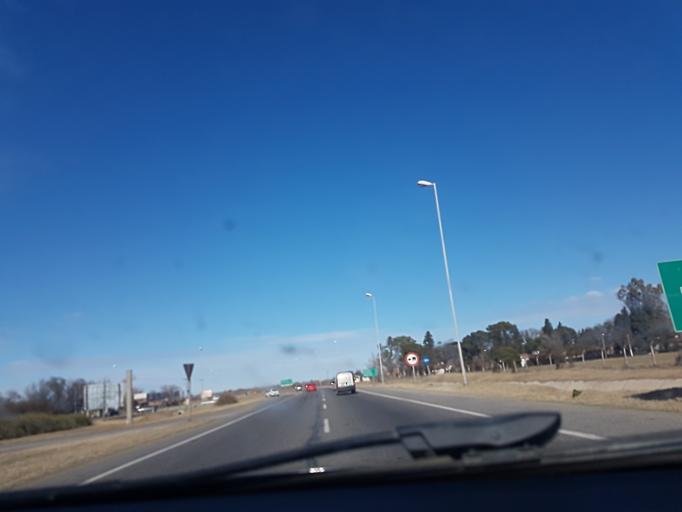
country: AR
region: Cordoba
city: La Calera
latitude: -31.3997
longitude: -64.2684
